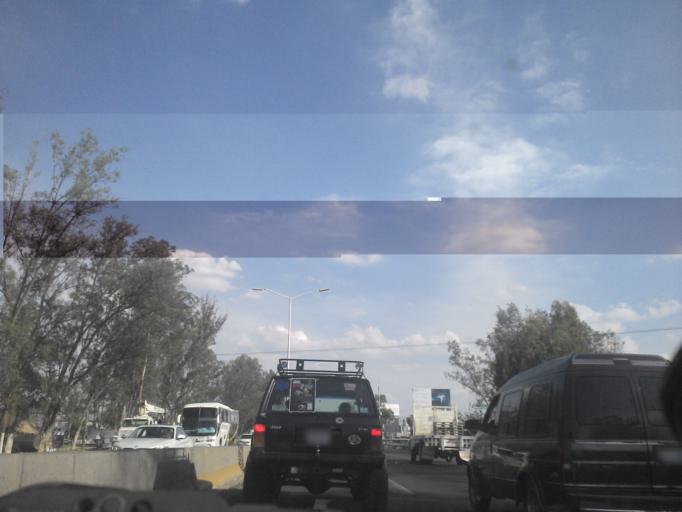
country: MX
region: Jalisco
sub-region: Tlajomulco de Zuniga
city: La Tijera
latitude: 20.6197
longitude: -103.4306
